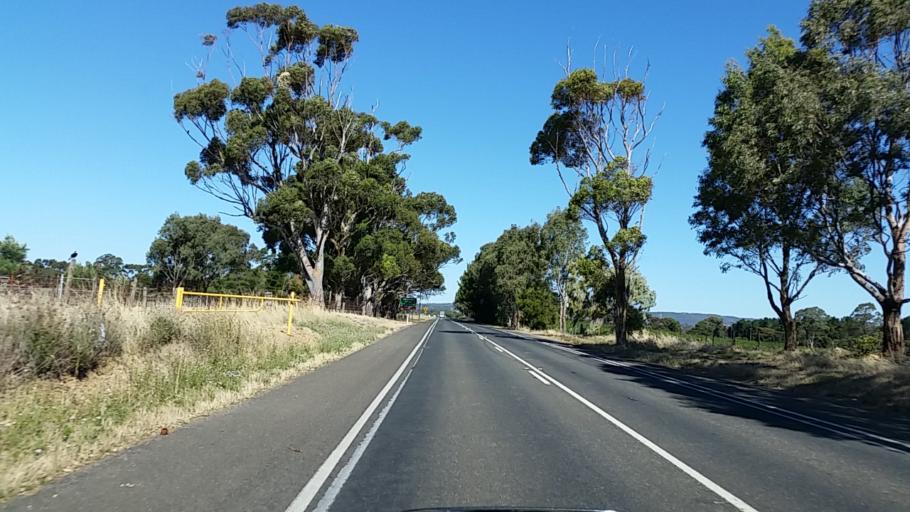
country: AU
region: South Australia
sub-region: Playford
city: One Tree Hill
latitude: -34.7157
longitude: 138.7400
